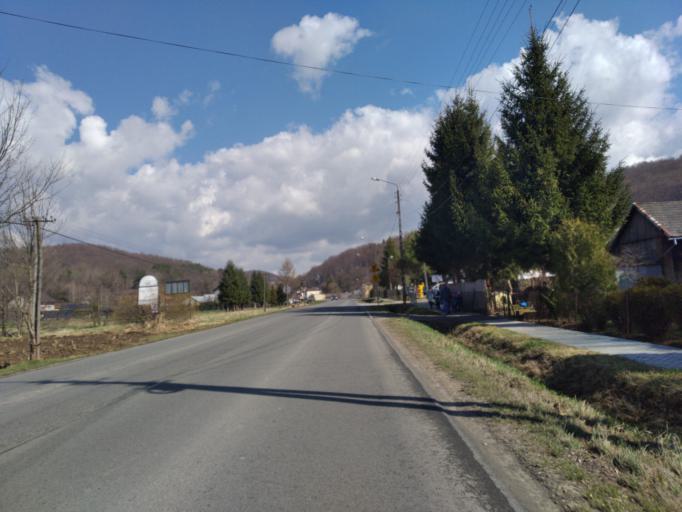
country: PL
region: Subcarpathian Voivodeship
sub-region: Powiat brzozowski
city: Grabownica Starzenska
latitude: 49.6638
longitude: 22.0816
